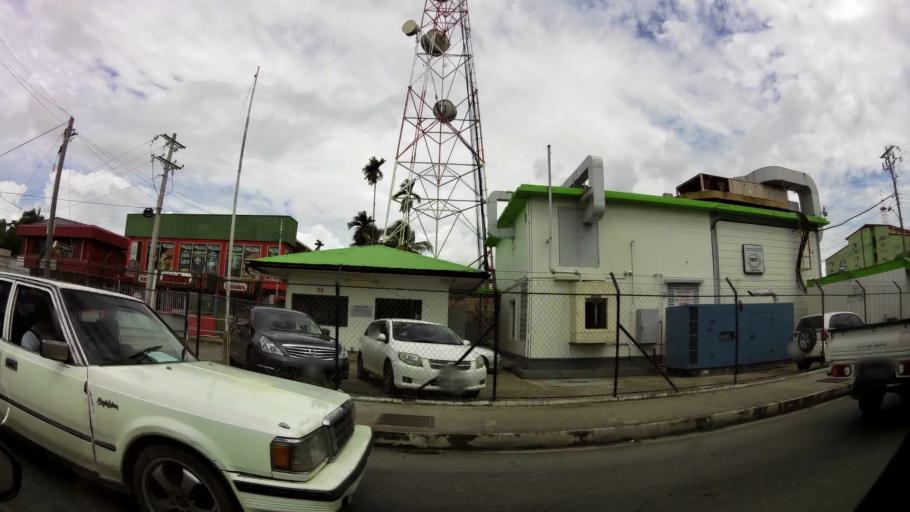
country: TT
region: Couva-Tabaquite-Talparo
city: Couva
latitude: 10.4221
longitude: -61.4597
